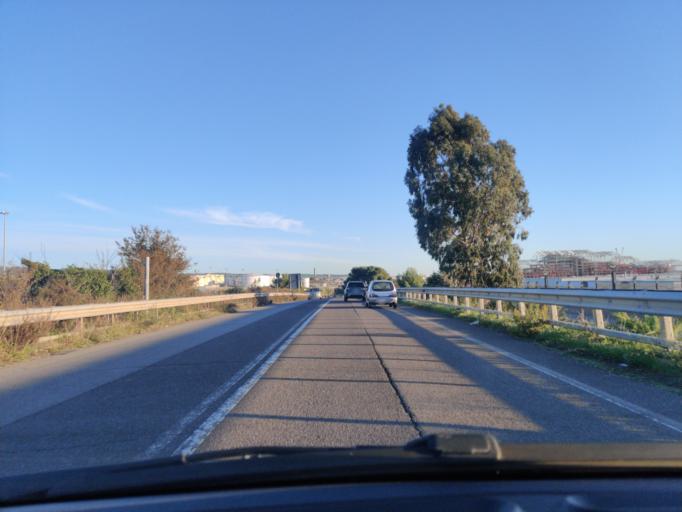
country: IT
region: Latium
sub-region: Citta metropolitana di Roma Capitale
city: Aurelia
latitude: 42.1149
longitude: 11.7729
